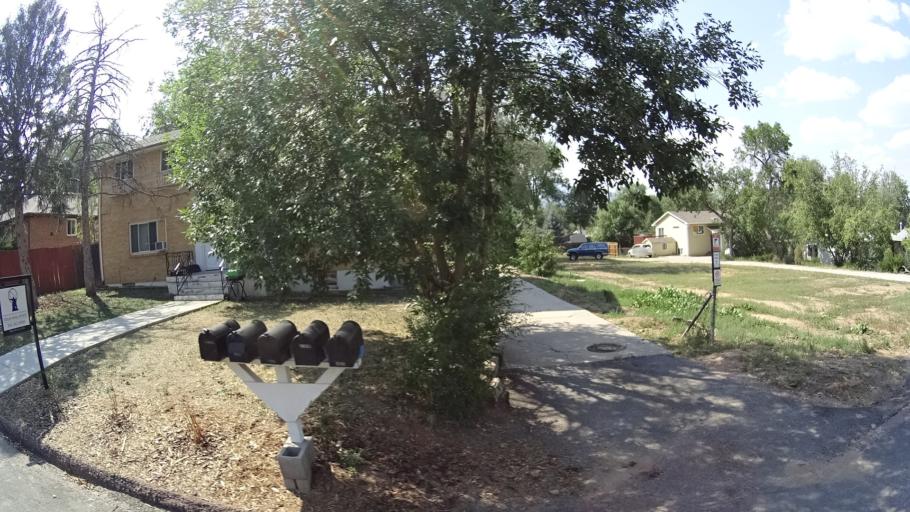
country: US
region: Colorado
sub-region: El Paso County
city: Colorado Springs
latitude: 38.8056
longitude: -104.8240
